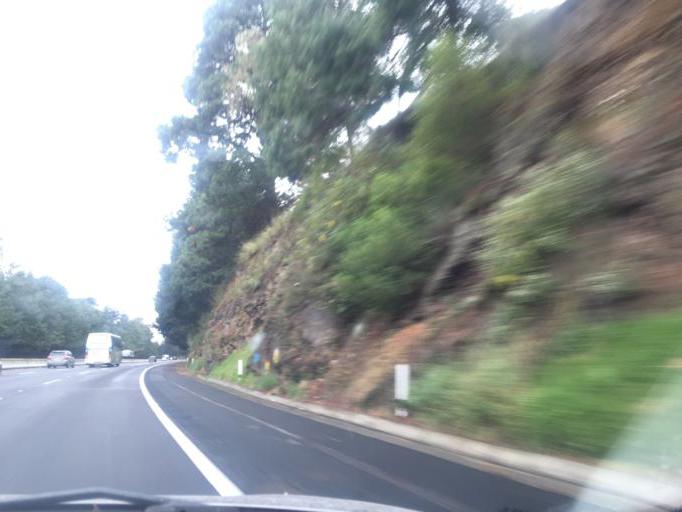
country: MX
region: Mexico City
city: Xochimilco
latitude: 19.1835
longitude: -99.1560
